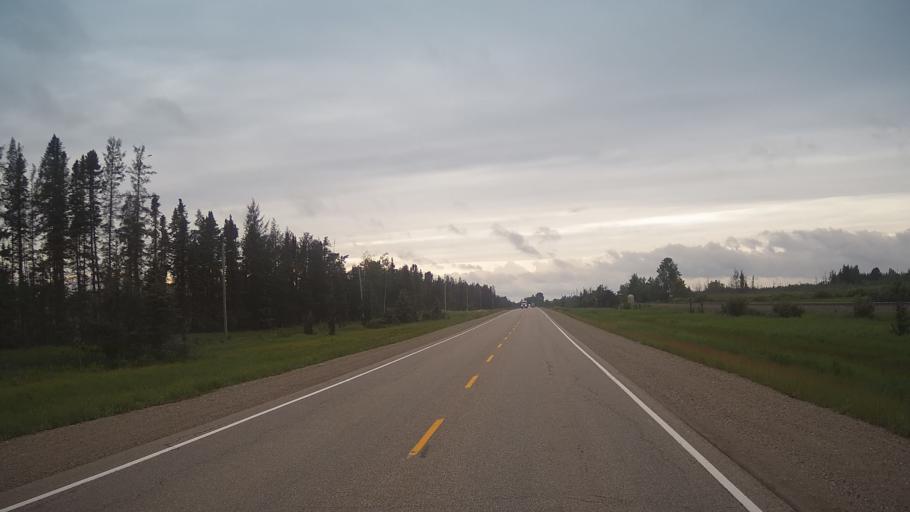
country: CA
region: Ontario
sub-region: Thunder Bay District
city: Thunder Bay
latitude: 48.8773
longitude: -89.9849
